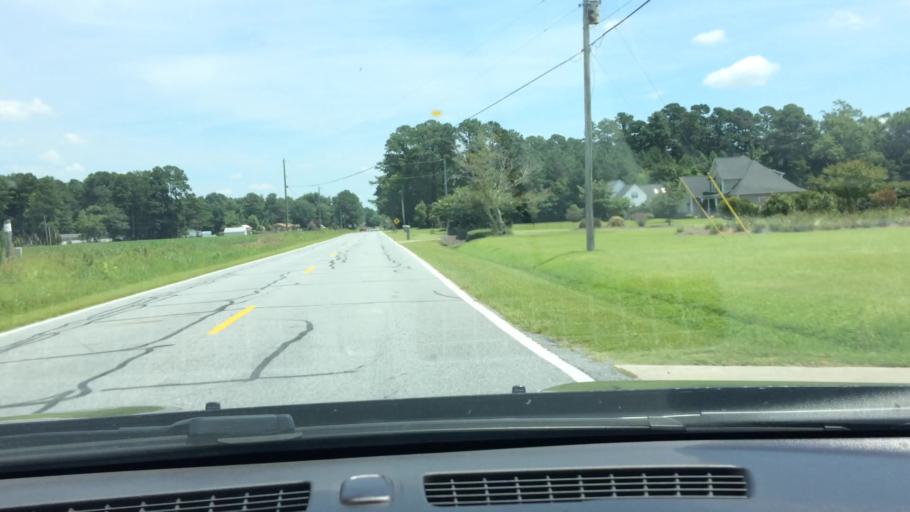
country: US
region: North Carolina
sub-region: Pitt County
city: Windsor
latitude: 35.5017
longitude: -77.3306
